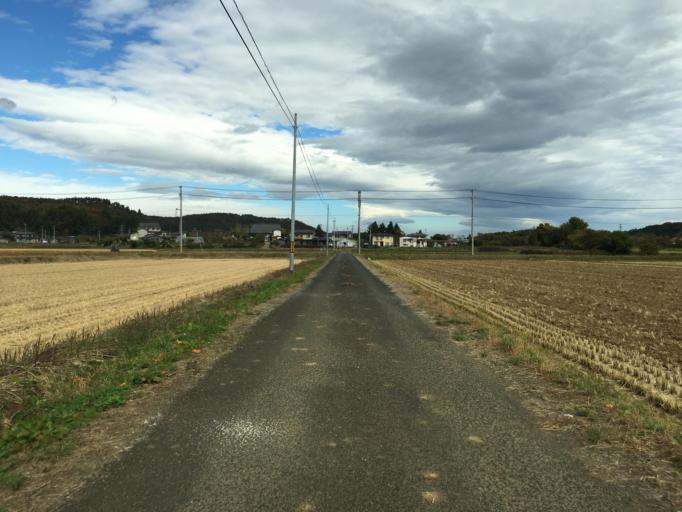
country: JP
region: Fukushima
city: Nihommatsu
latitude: 37.6491
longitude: 140.4444
